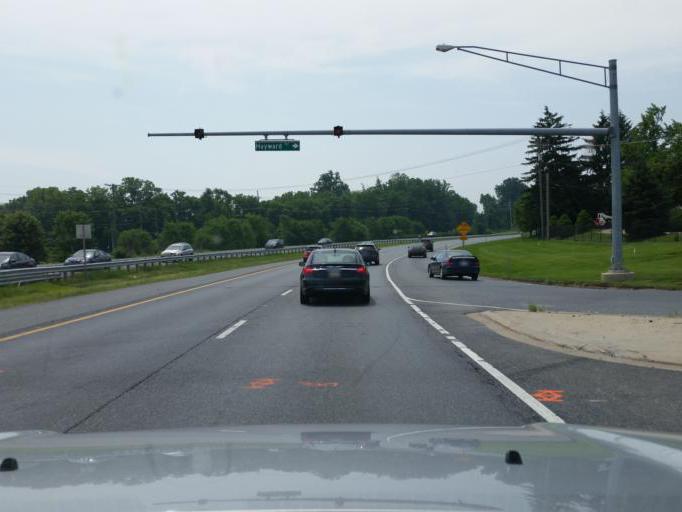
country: US
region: Maryland
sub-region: Frederick County
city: Clover Hill
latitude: 39.4561
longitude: -77.3997
